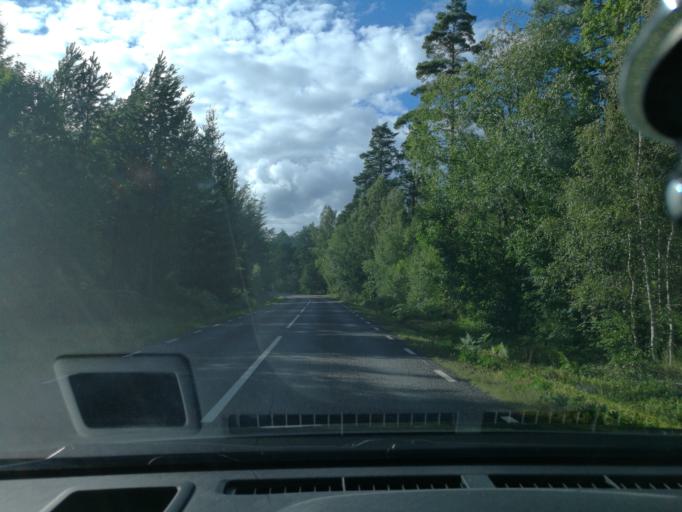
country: SE
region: Kronoberg
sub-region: Vaxjo Kommun
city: Braas
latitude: 57.0620
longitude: 15.0318
